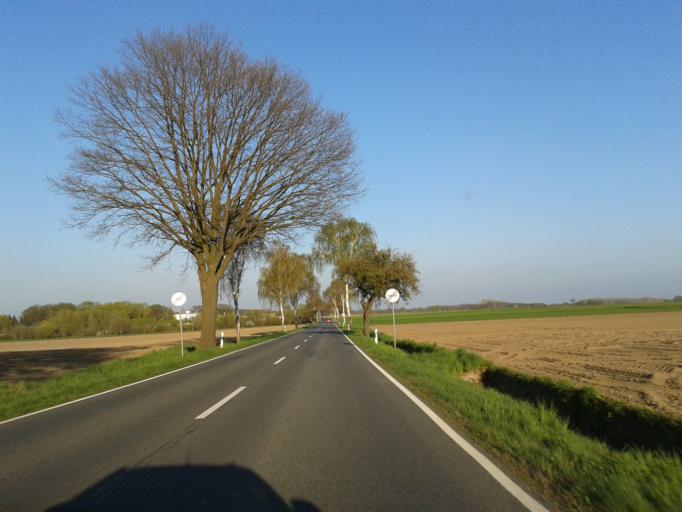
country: DE
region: Lower Saxony
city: Kusten
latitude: 52.9362
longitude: 11.0256
